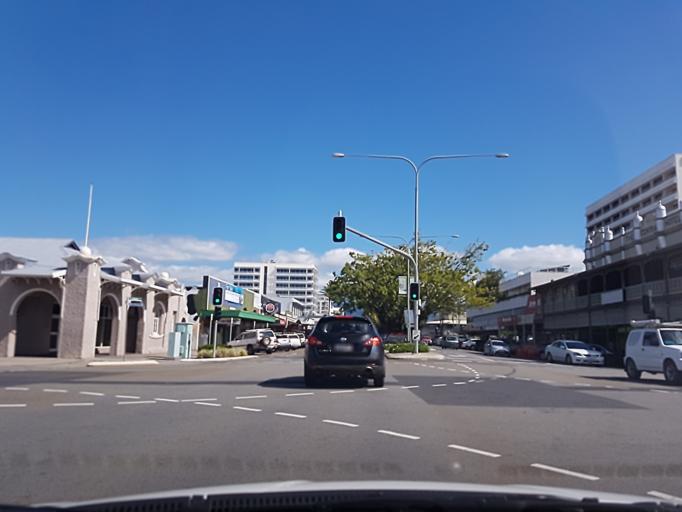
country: AU
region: Queensland
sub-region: Cairns
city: Cairns
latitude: -16.9238
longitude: 145.7773
